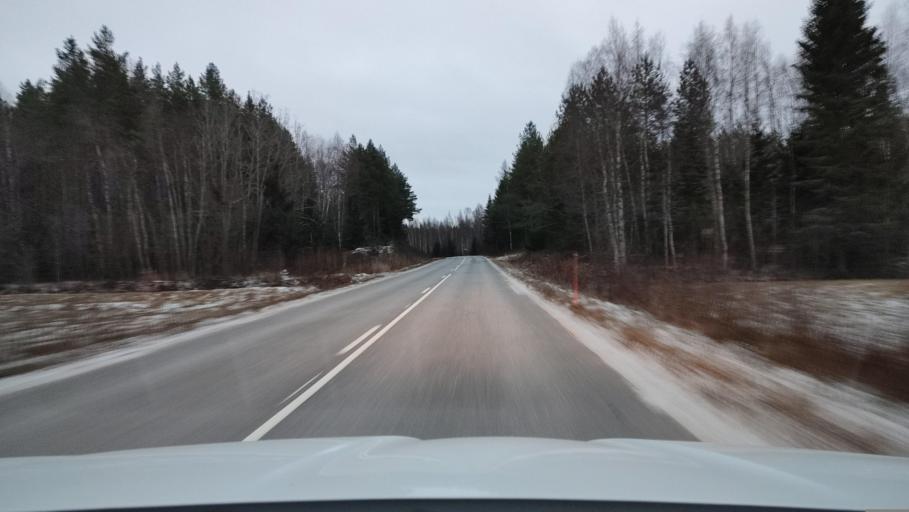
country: FI
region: Ostrobothnia
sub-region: Vaasa
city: Replot
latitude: 63.2409
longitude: 21.3847
